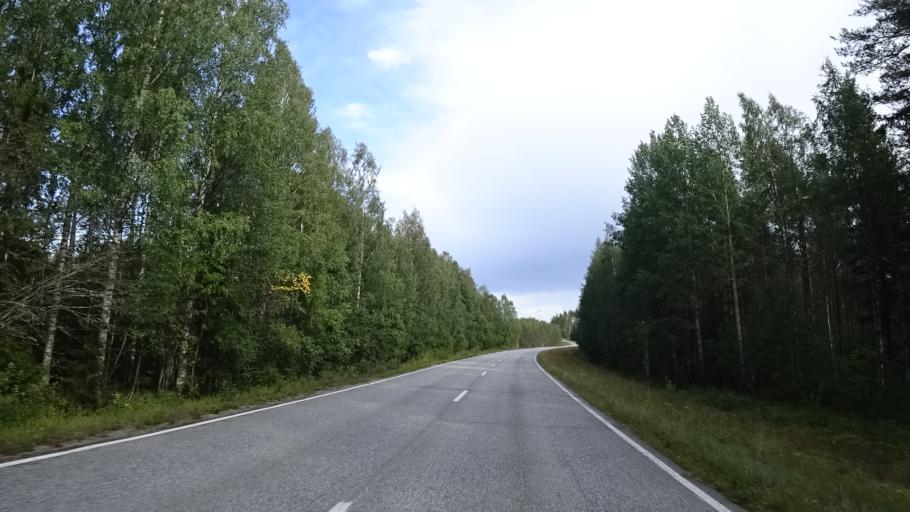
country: FI
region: North Karelia
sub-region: Joensuu
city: Ilomantsi
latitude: 62.6221
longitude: 31.1604
